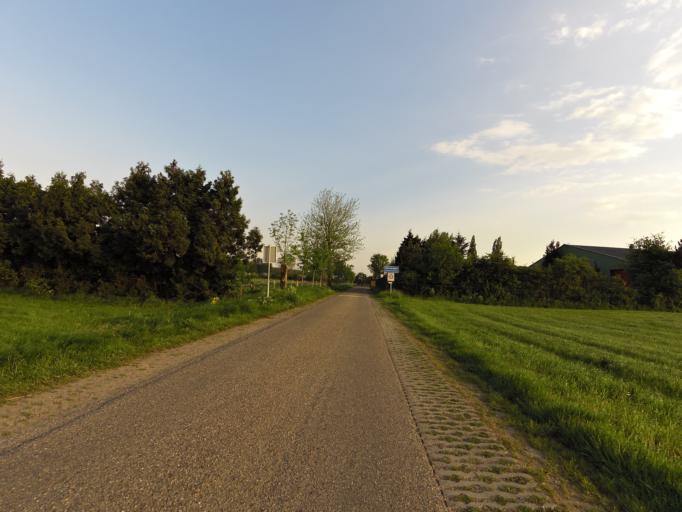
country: NL
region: Gelderland
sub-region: Oude IJsselstreek
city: Gendringen
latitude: 51.8569
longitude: 6.3177
